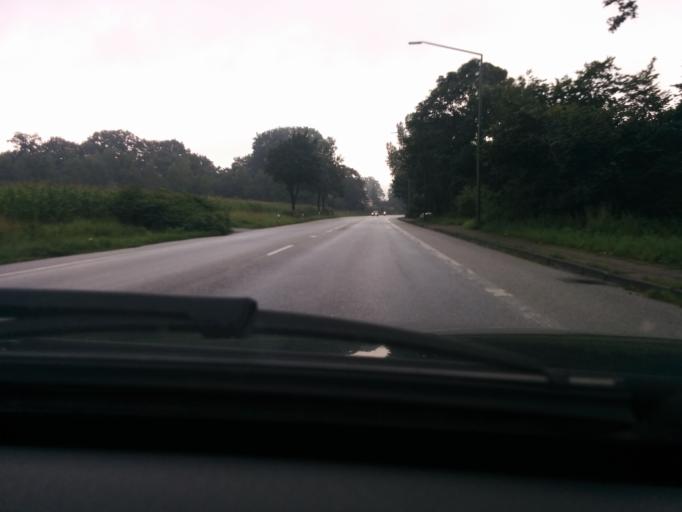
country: DE
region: North Rhine-Westphalia
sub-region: Regierungsbezirk Detmold
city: Bielefeld
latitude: 52.0038
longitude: 8.4852
